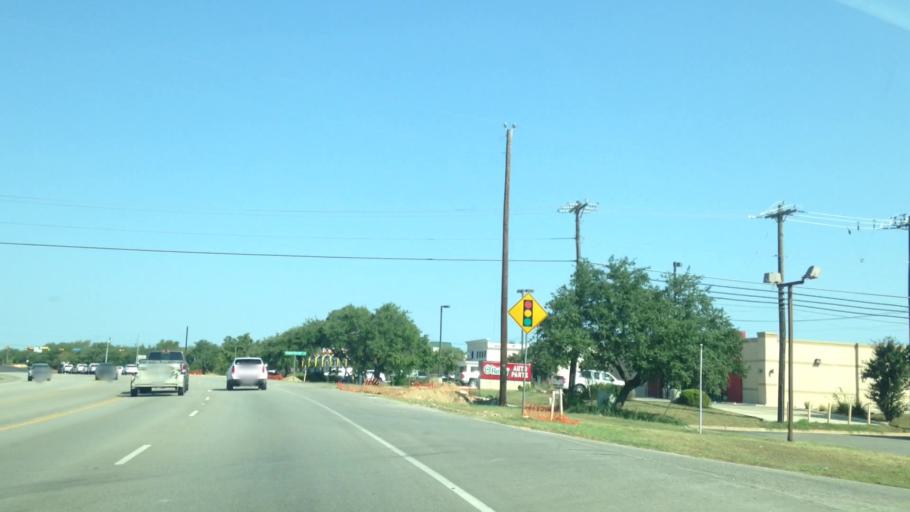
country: US
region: Texas
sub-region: Williamson County
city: Serenada
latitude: 30.6721
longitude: -97.6994
